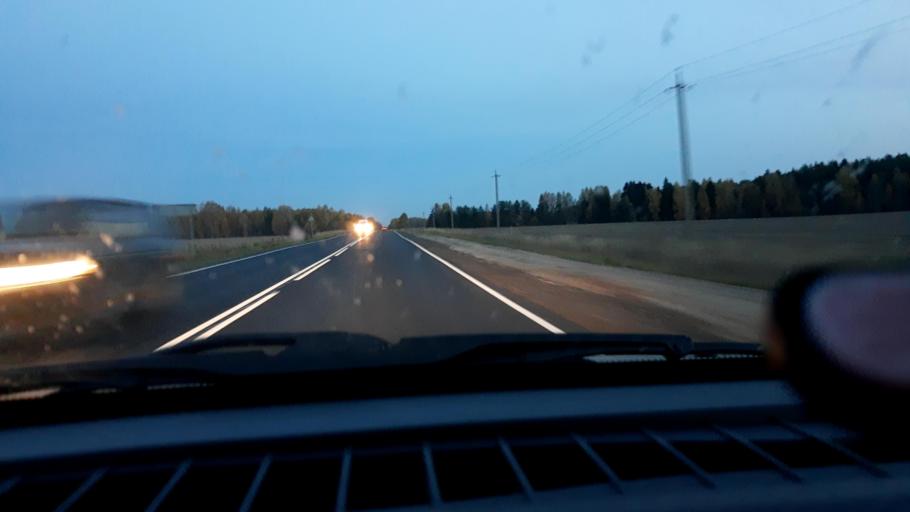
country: RU
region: Nizjnij Novgorod
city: Novaya Balakhna
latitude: 56.5965
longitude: 43.6447
